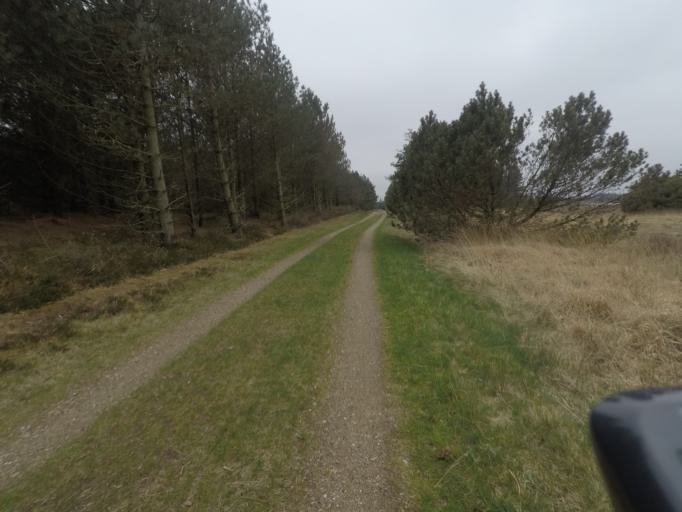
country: DE
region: Schleswig-Holstein
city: List
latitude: 55.1234
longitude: 8.5347
